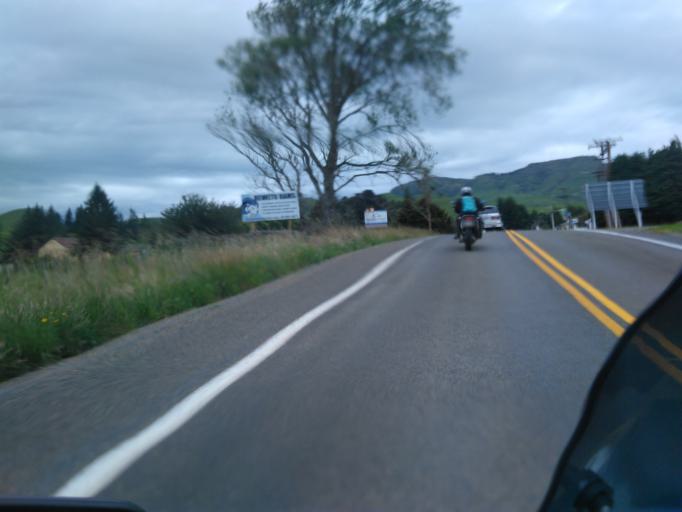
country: NZ
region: Bay of Plenty
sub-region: Opotiki District
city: Opotiki
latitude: -38.3580
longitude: 177.5328
